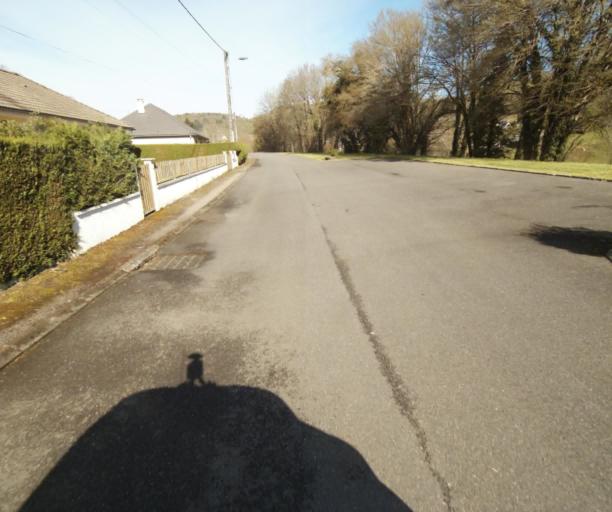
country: FR
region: Limousin
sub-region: Departement de la Correze
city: Laguenne
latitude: 45.2526
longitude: 1.8389
